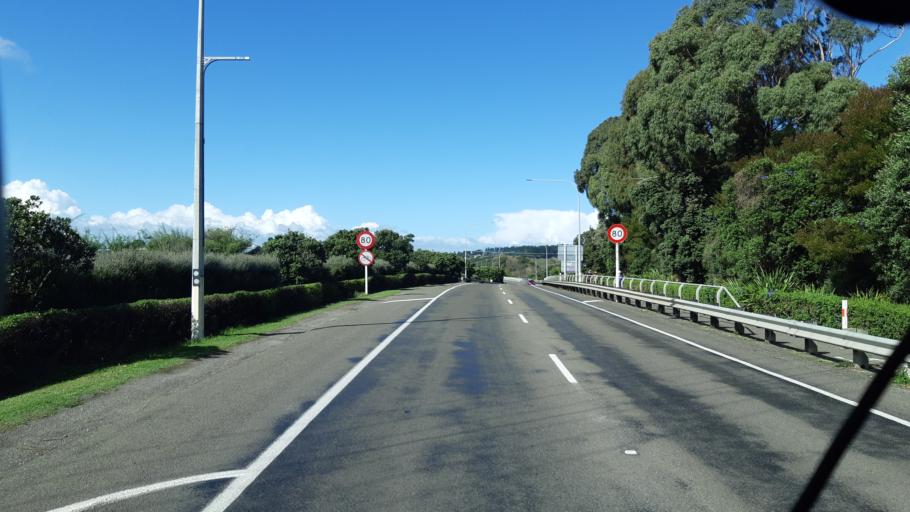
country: NZ
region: Manawatu-Wanganui
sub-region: Wanganui District
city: Wanganui
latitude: -39.9422
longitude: 175.0430
